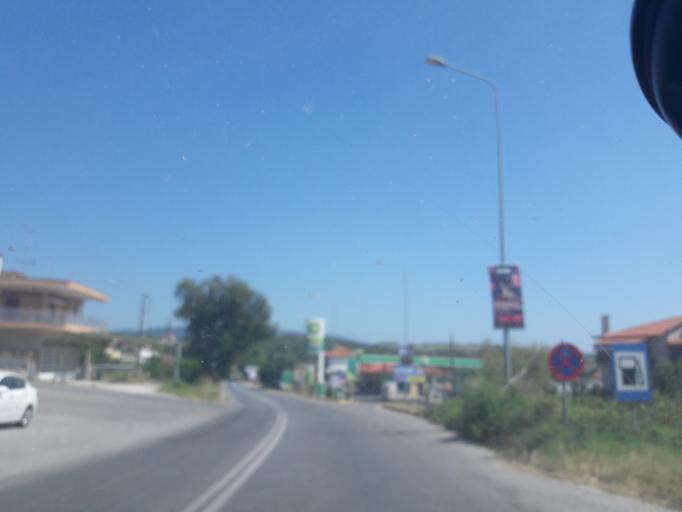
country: GR
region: Central Macedonia
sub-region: Nomos Chalkidikis
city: Nea Roda
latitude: 40.3796
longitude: 23.9212
